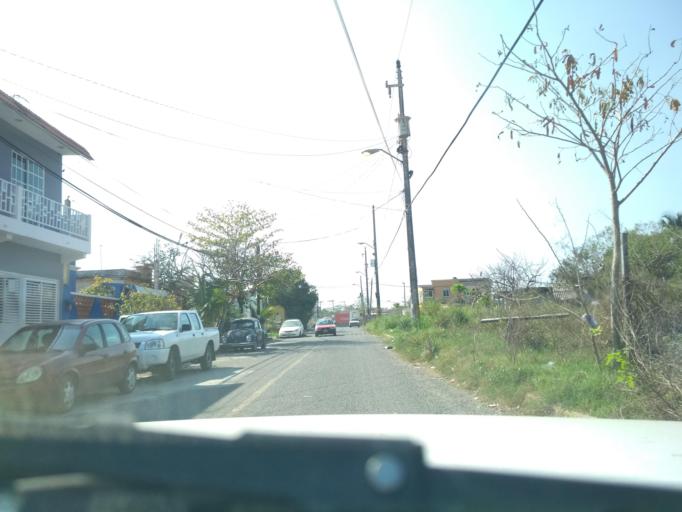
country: MX
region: Veracruz
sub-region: Veracruz
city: Colonia Chalchihuecan
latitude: 19.2172
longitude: -96.2130
